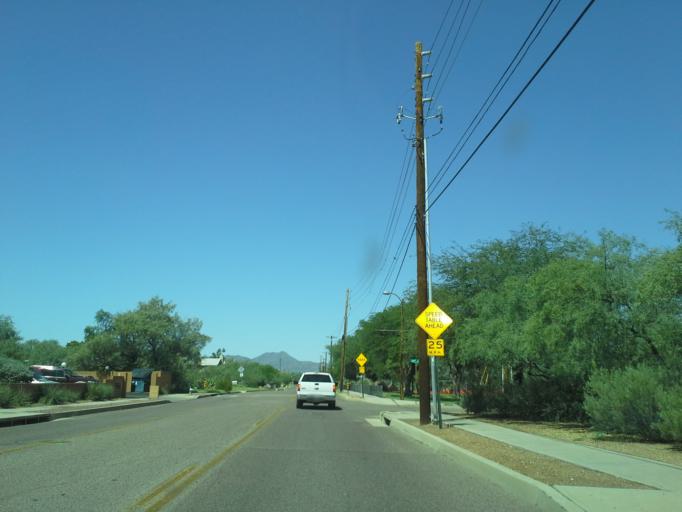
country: US
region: Arizona
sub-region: Pima County
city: Flowing Wells
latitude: 32.2830
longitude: -110.9648
